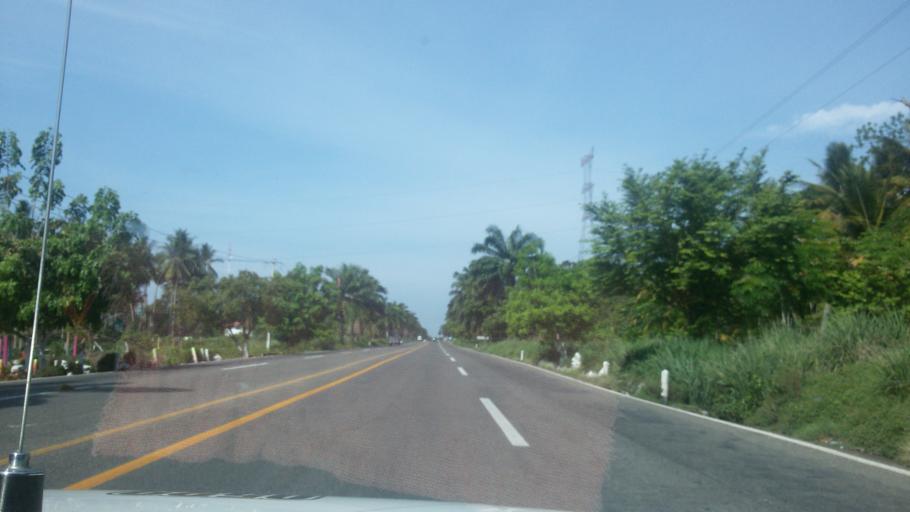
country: MX
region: Chiapas
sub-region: Tapachula
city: Llano de la Lima
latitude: 14.8530
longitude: -92.3037
